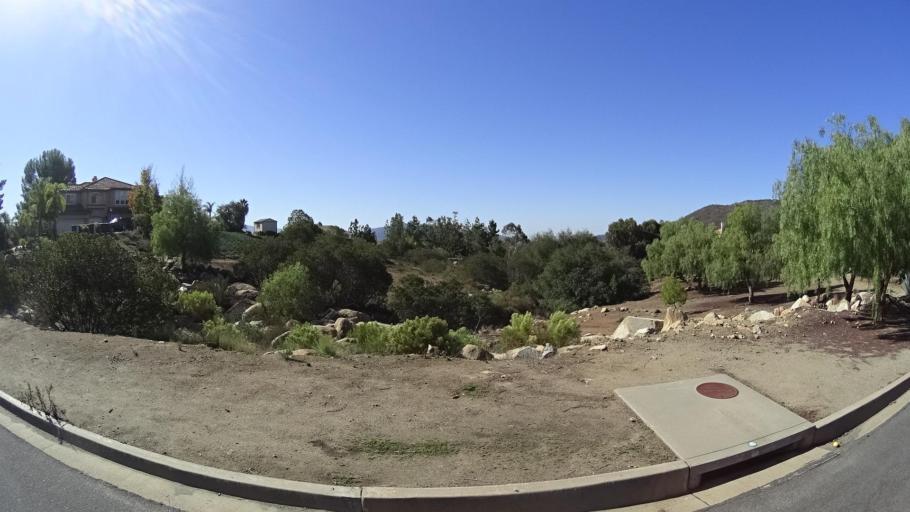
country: US
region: California
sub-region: San Diego County
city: Jamul
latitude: 32.7394
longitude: -116.8583
